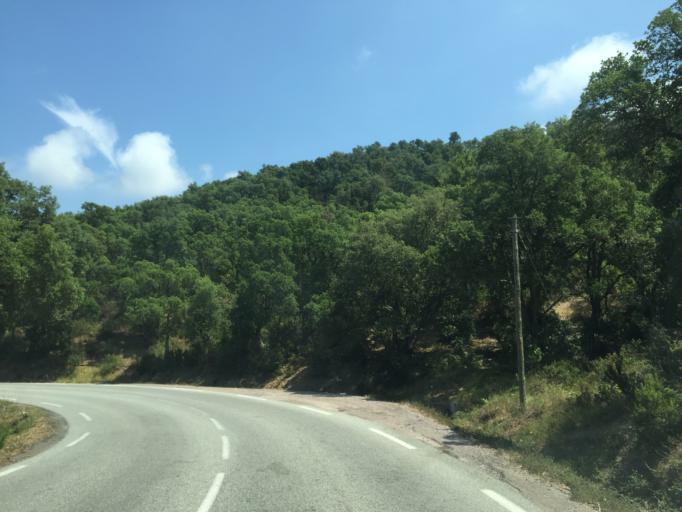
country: FR
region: Provence-Alpes-Cote d'Azur
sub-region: Departement du Var
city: Sainte-Maxime
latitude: 43.3668
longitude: 6.6761
